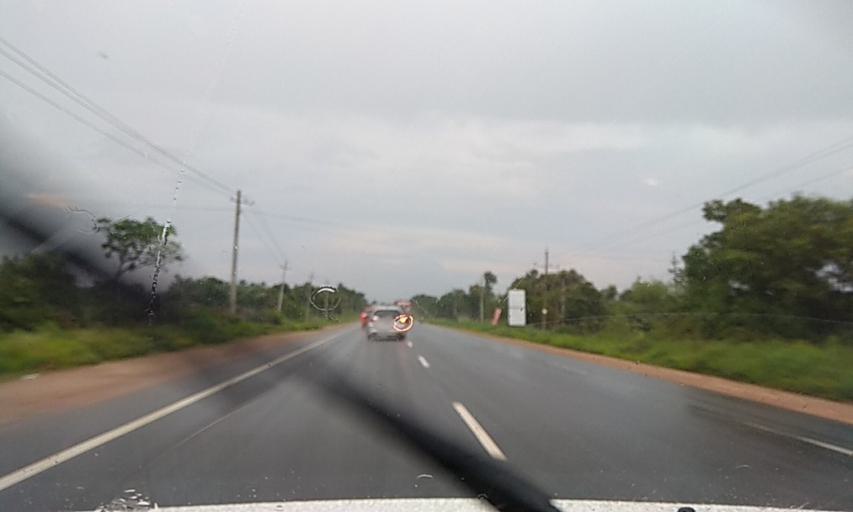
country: IN
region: Karnataka
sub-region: Mysore
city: Nanjangud
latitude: 12.0331
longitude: 76.6742
